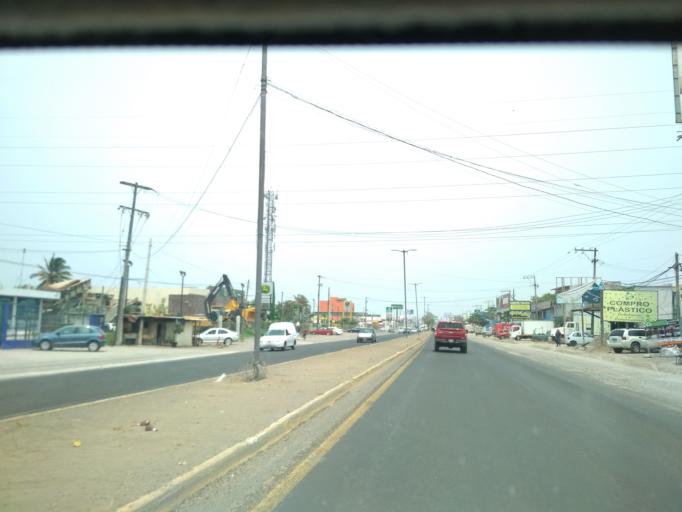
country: MX
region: Veracruz
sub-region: Veracruz
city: Las Amapolas
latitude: 19.1613
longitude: -96.2048
